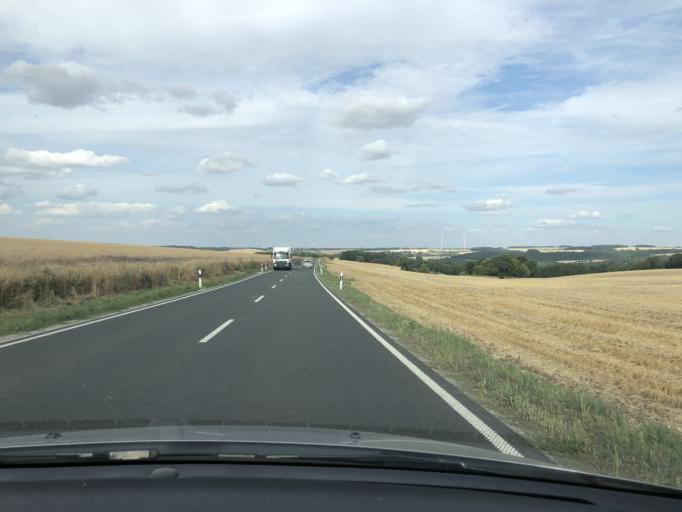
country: DE
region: Thuringia
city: Schmiedehausen
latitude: 51.0516
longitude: 11.6676
